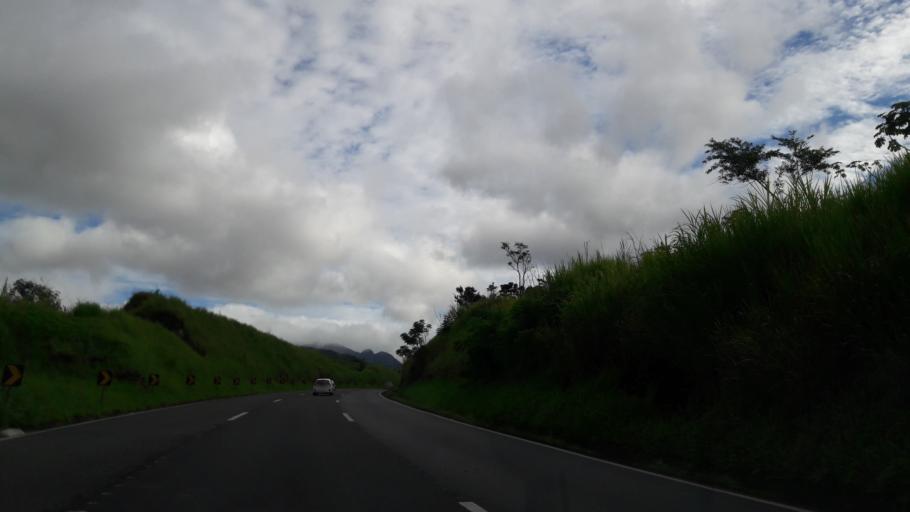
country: BR
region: Sao Paulo
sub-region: Cajati
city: Cajati
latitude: -24.7983
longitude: -48.2153
